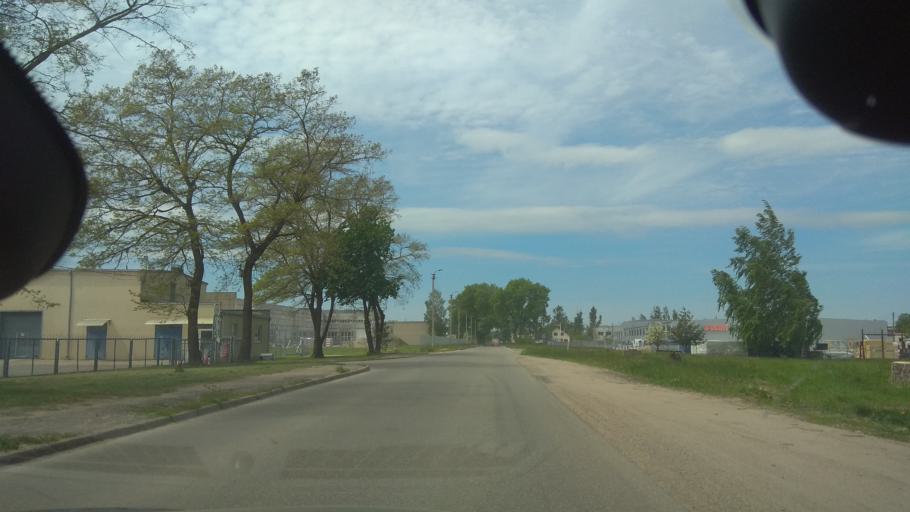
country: LT
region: Kauno apskritis
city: Jonava
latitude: 55.0904
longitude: 24.2858
